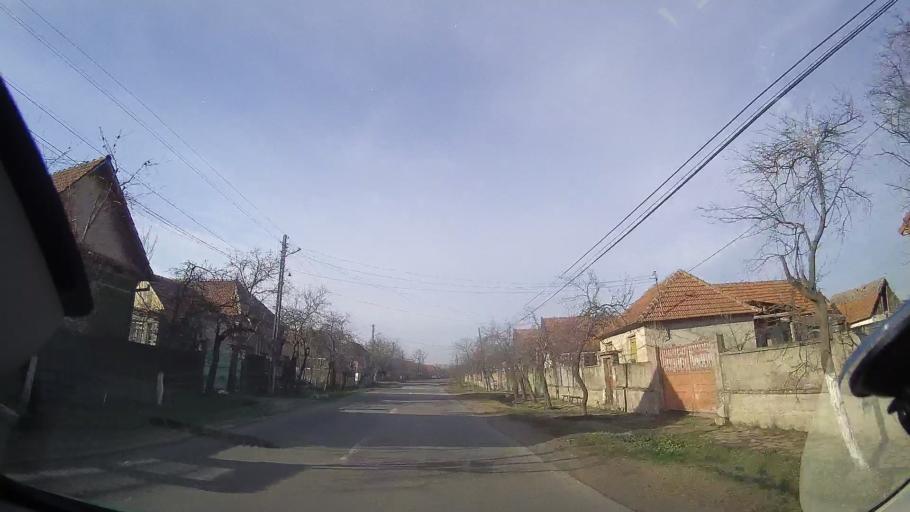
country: RO
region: Bihor
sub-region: Comuna Brusturi
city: Brusturi
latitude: 47.1495
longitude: 22.2521
